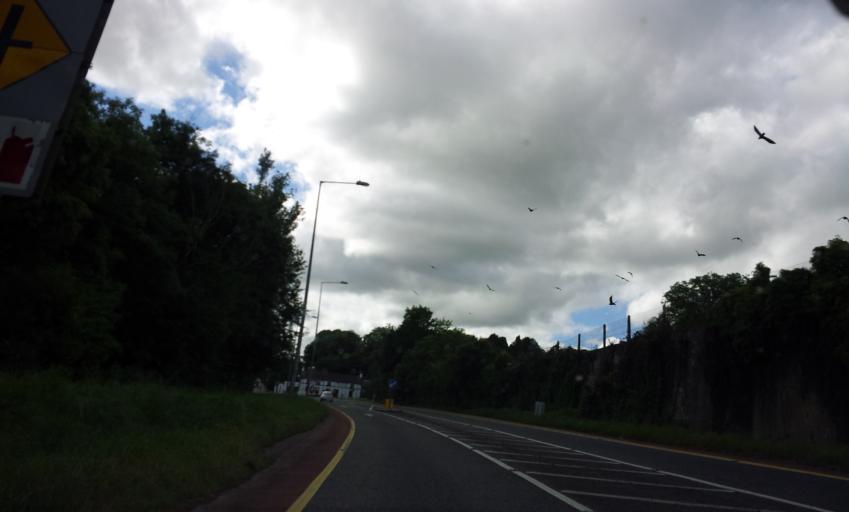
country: IE
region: Munster
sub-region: County Cork
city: Killumney
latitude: 51.8829
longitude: -8.6746
